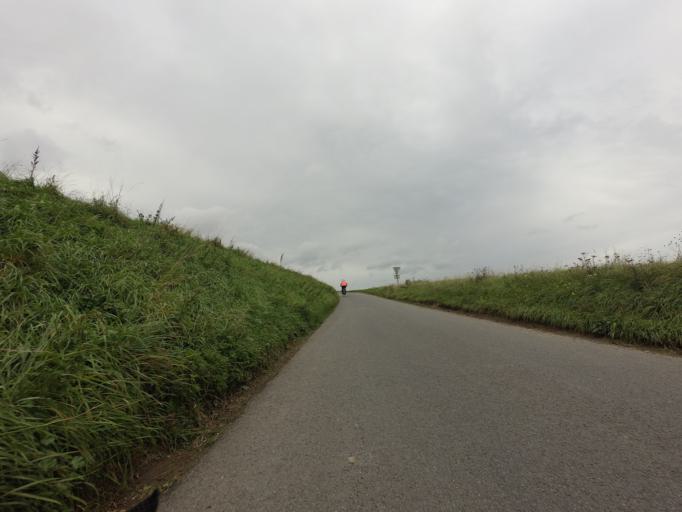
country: GB
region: England
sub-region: Cambridgeshire
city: Duxford
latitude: 52.0421
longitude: 0.1710
